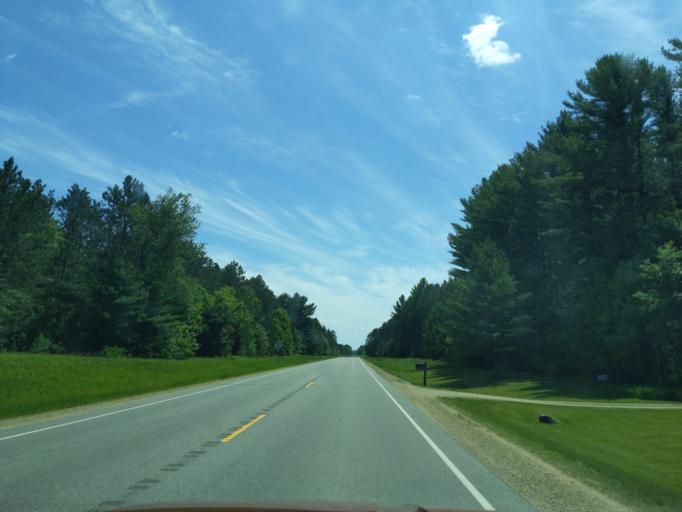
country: US
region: Wisconsin
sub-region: Marquette County
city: Montello
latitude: 43.9144
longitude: -89.3122
